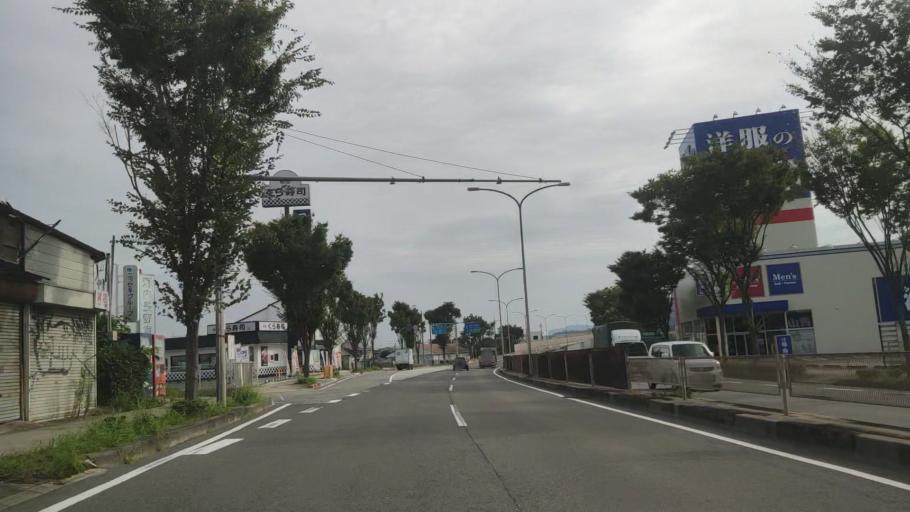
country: JP
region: Osaka
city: Tondabayashicho
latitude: 34.4570
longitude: 135.5649
